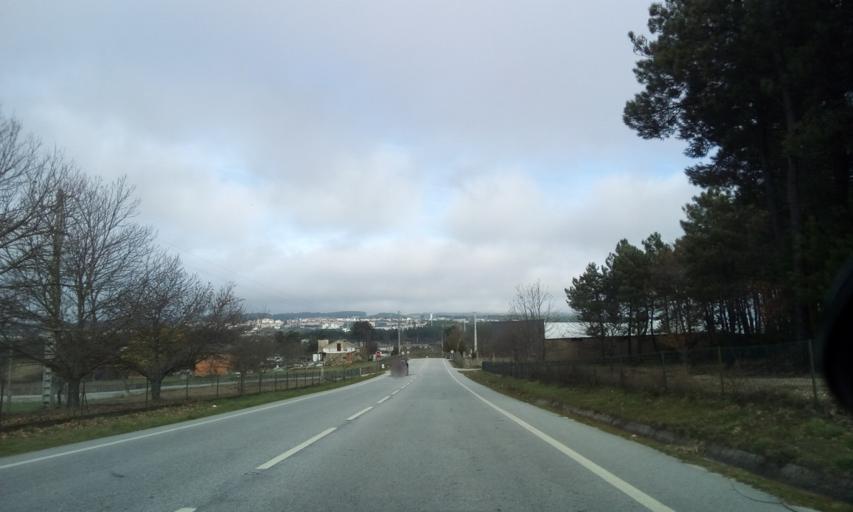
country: PT
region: Guarda
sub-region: Aguiar da Beira
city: Aguiar da Beira
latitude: 40.8046
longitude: -7.5250
